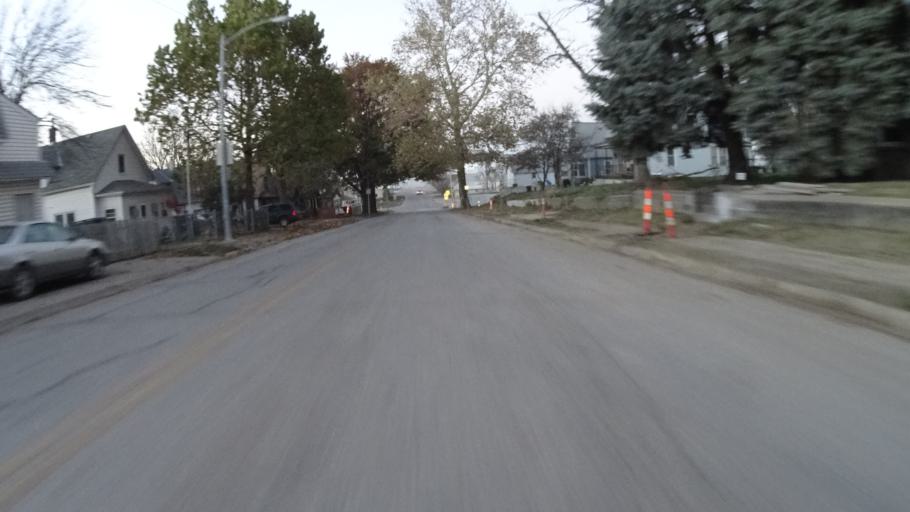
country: US
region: Nebraska
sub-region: Douglas County
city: Omaha
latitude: 41.2162
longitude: -95.9625
